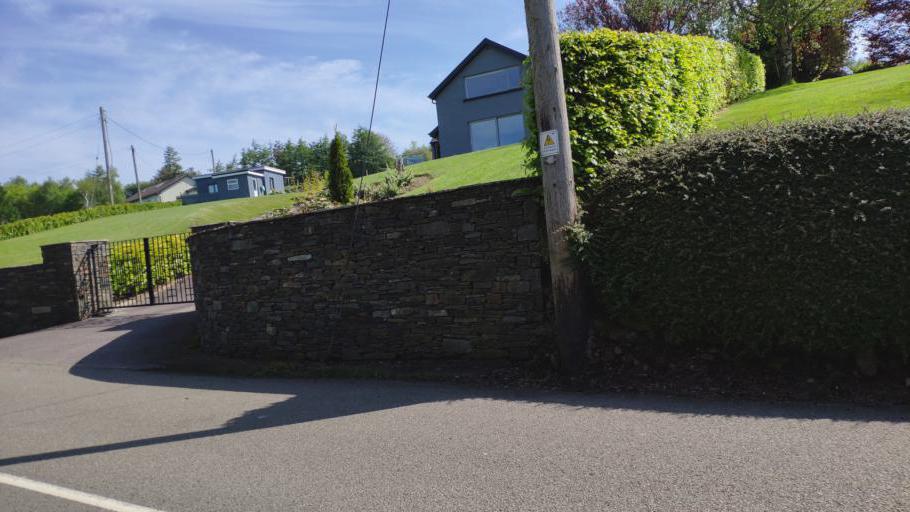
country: IE
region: Munster
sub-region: County Cork
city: Blarney
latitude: 51.9561
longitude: -8.5753
